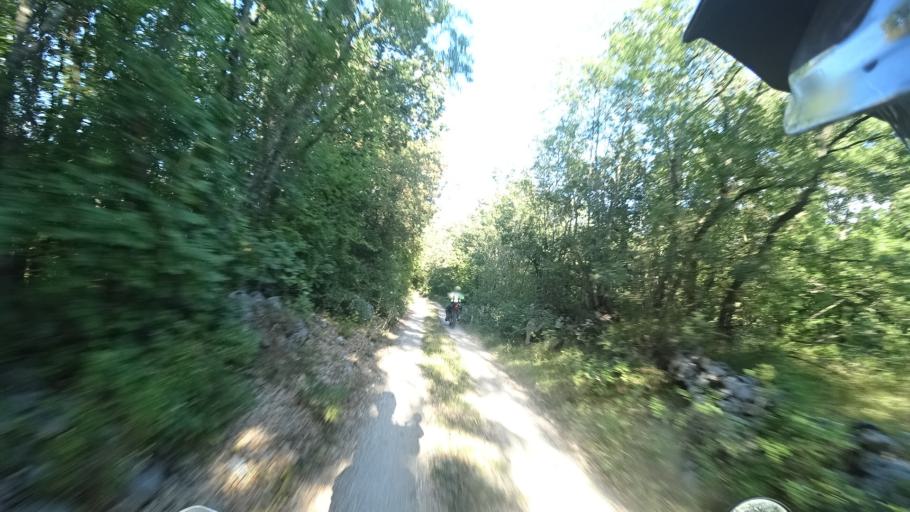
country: HR
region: Sibensko-Kniniska
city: Knin
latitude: 44.1653
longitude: 16.0846
